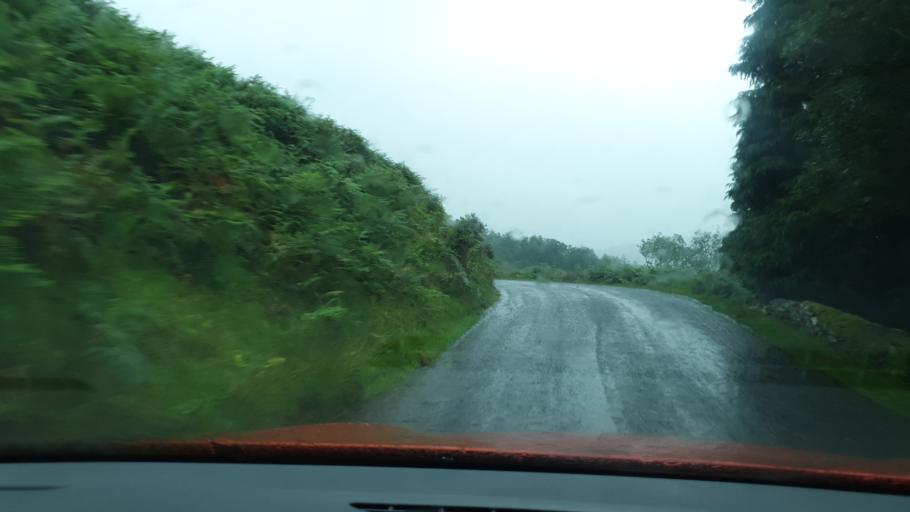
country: GB
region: England
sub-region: Cumbria
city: Millom
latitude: 54.3106
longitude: -3.2280
